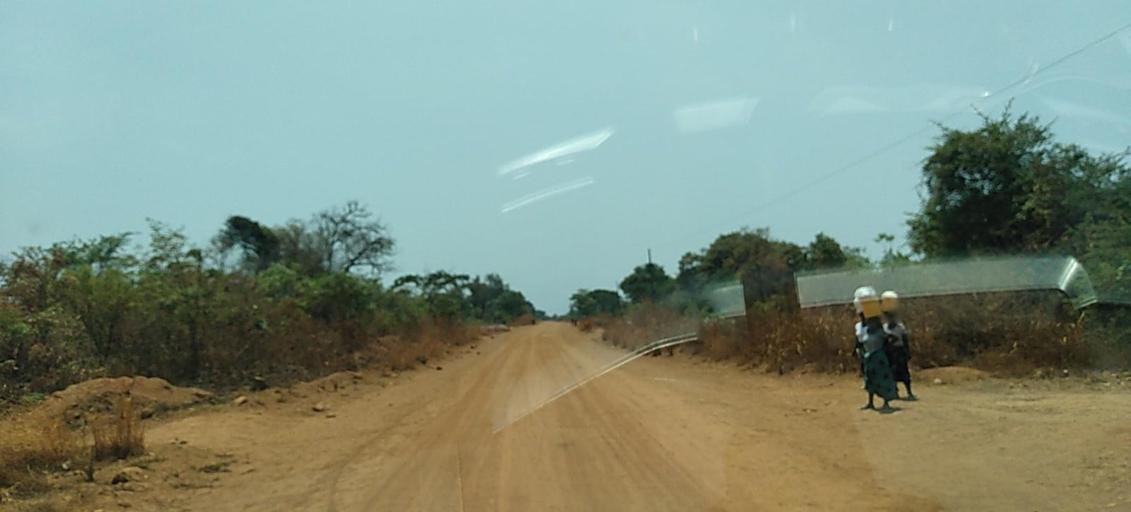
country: CD
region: Katanga
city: Kipushi
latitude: -11.9345
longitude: 26.9693
